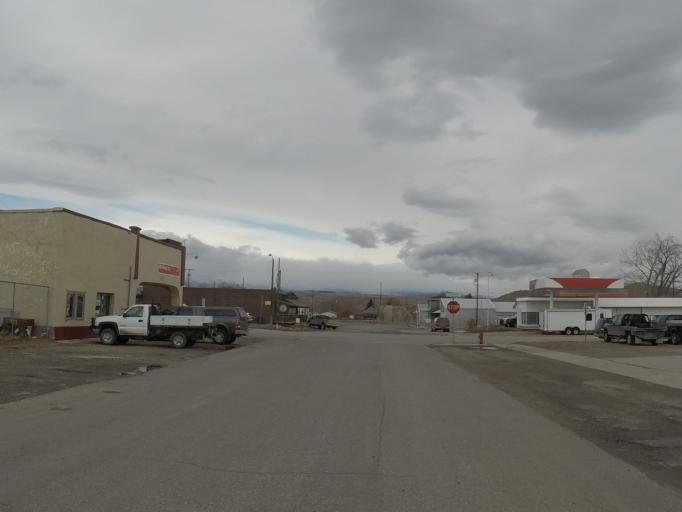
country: US
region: Montana
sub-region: Sweet Grass County
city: Big Timber
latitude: 45.8352
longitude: -109.9538
